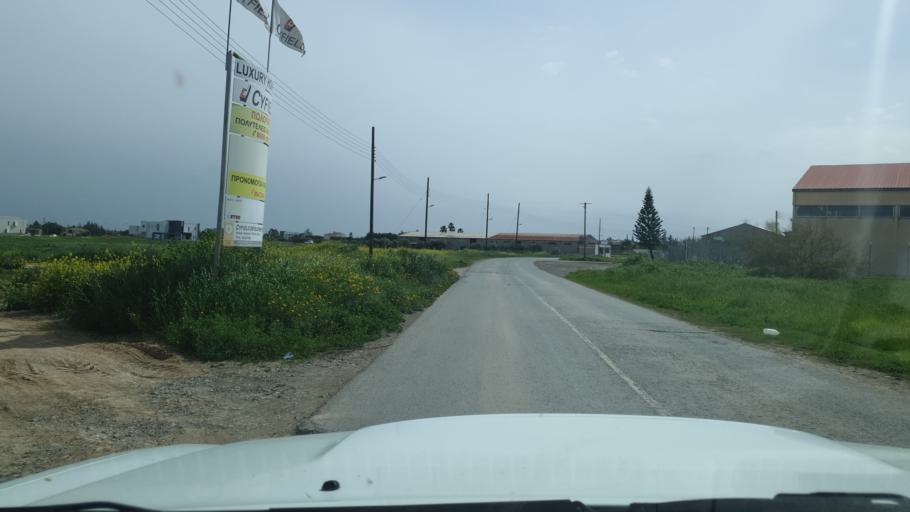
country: CY
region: Lefkosia
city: Geri
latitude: 35.0874
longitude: 33.3864
